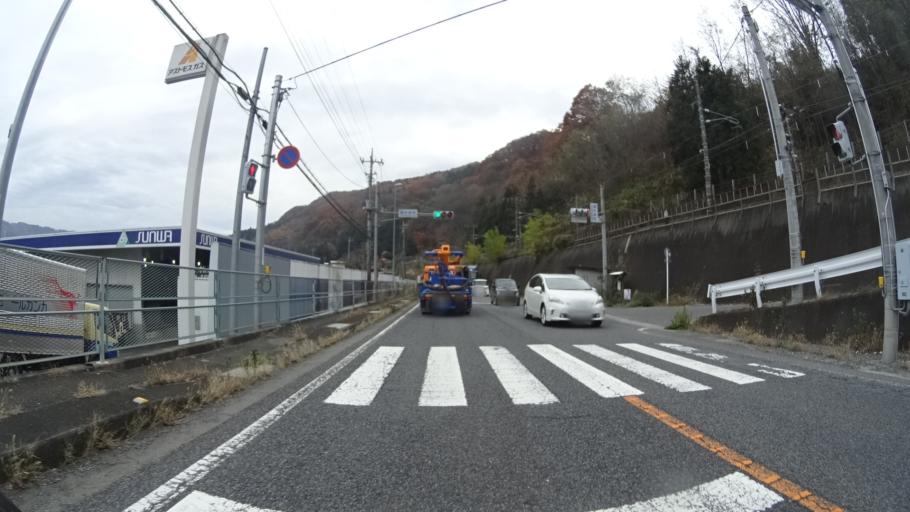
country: JP
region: Gunma
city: Numata
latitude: 36.6124
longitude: 139.0417
